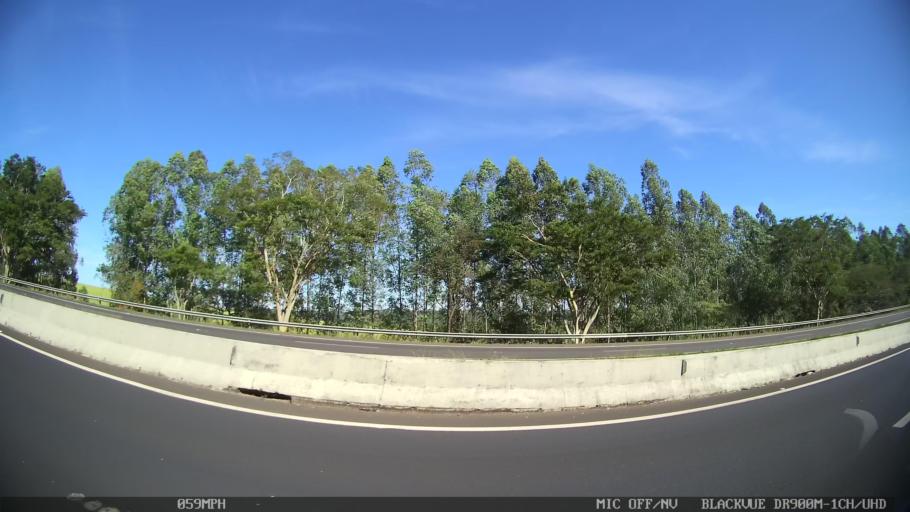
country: BR
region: Sao Paulo
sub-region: Santa Rita Do Passa Quatro
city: Santa Rita do Passa Quatro
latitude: -21.7525
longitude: -47.5681
